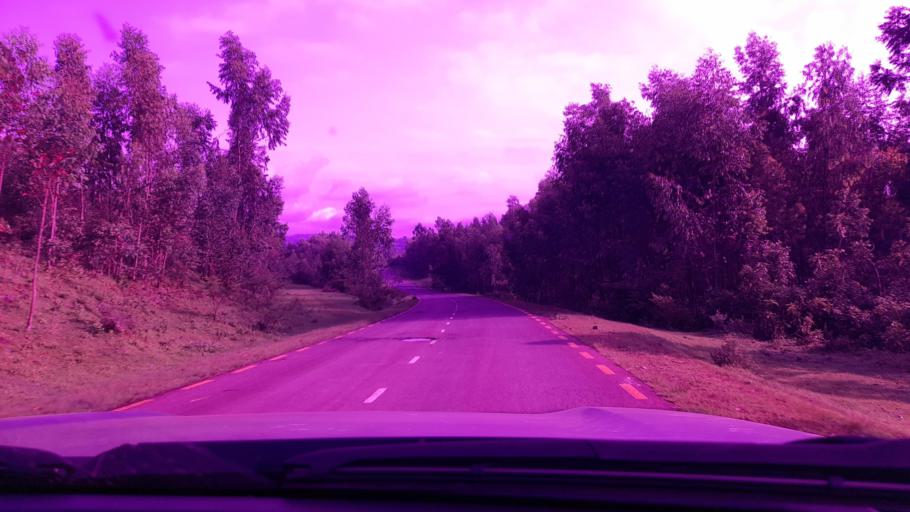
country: ET
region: Oromiya
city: Bedele
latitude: 8.1973
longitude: 36.4437
